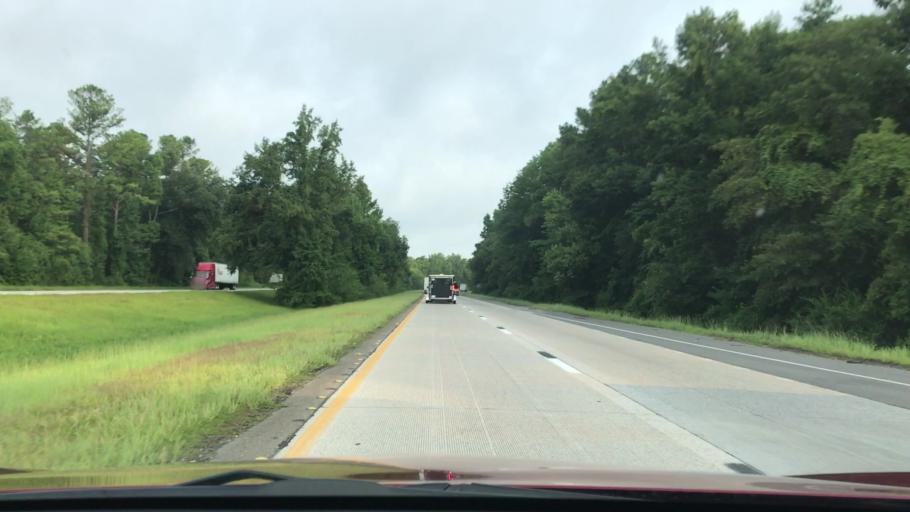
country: US
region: South Carolina
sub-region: Orangeburg County
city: Holly Hill
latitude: 33.2343
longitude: -80.4511
